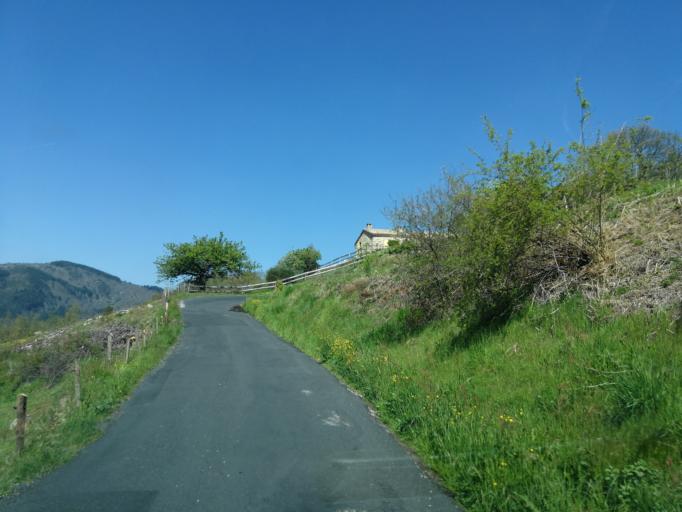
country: FR
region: Rhone-Alpes
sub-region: Departement de l'Ardeche
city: Le Cheylard
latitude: 44.9227
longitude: 4.4195
